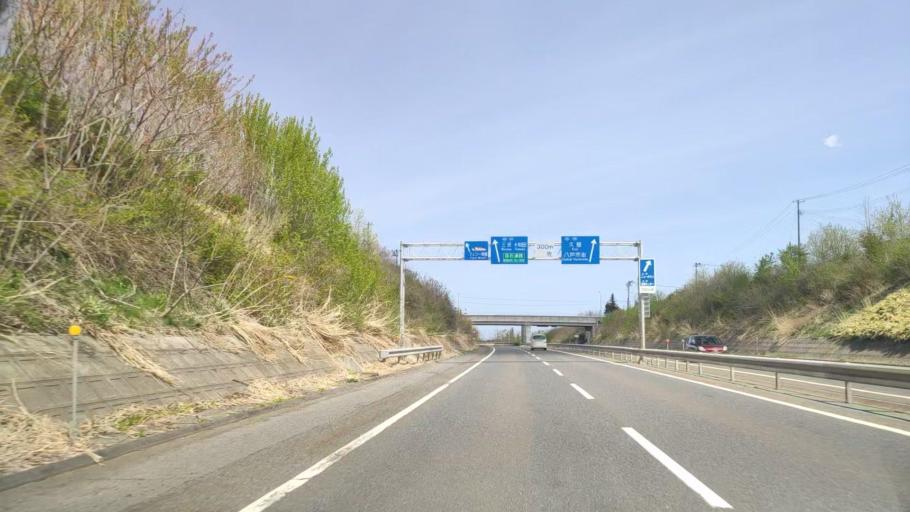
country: JP
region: Aomori
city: Hachinohe
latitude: 40.4888
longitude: 141.4638
